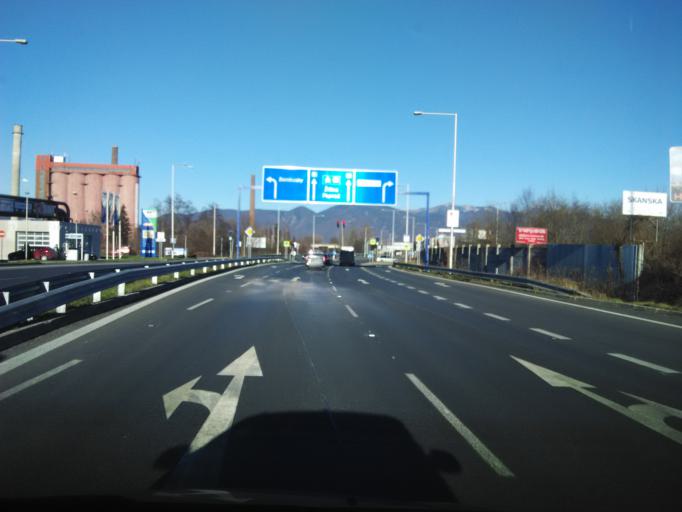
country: SK
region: Zilinsky
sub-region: Okres Martin
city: Martin
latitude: 49.0617
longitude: 18.9093
